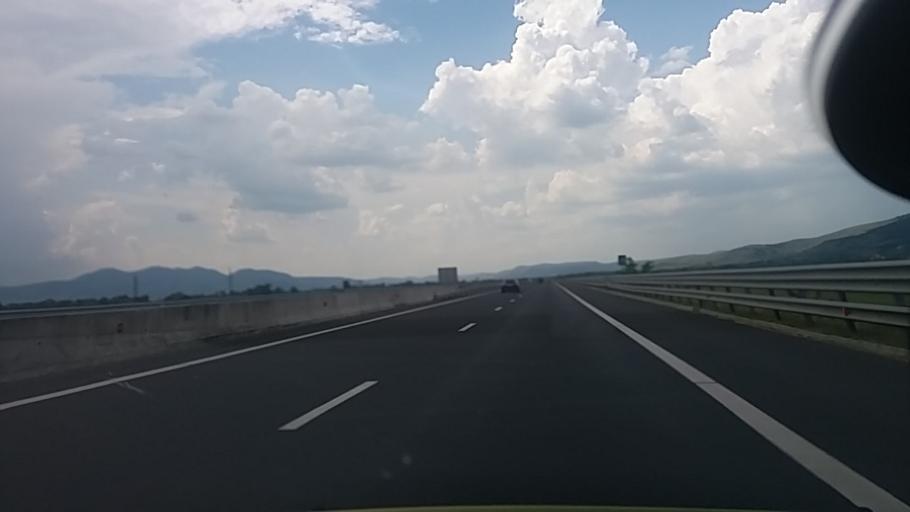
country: RO
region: Hunedoara
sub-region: Oras Simeria
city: Simeria
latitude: 45.8711
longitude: 23.0151
